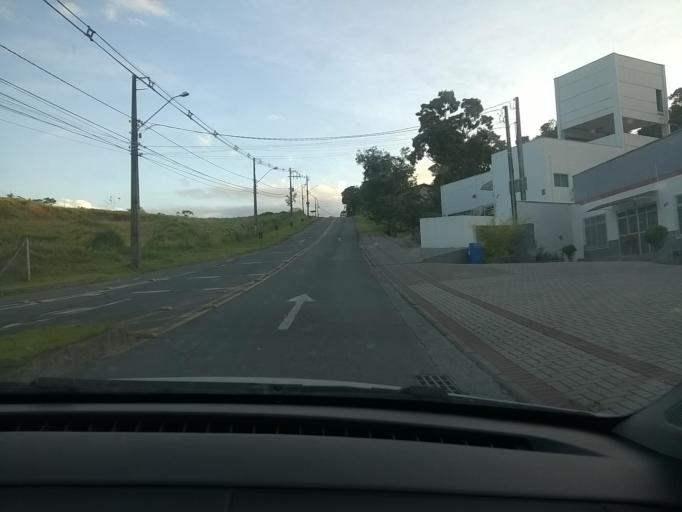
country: BR
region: Santa Catarina
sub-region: Blumenau
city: Blumenau
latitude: -26.9206
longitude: -49.1345
